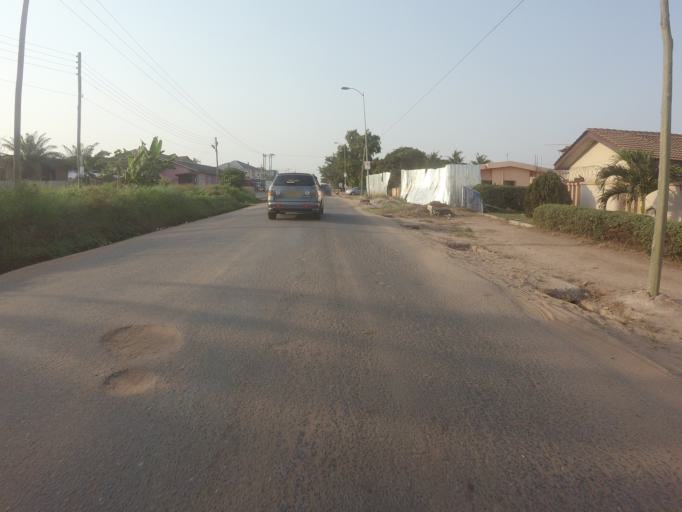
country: GH
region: Greater Accra
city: Nungua
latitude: 5.6168
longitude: -0.0523
